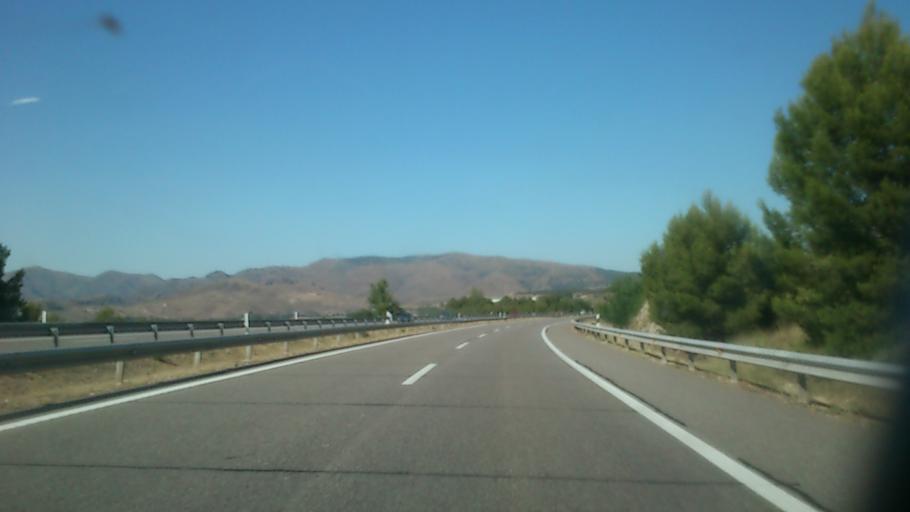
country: ES
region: Aragon
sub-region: Provincia de Zaragoza
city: Calatayud
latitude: 41.3462
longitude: -1.6283
